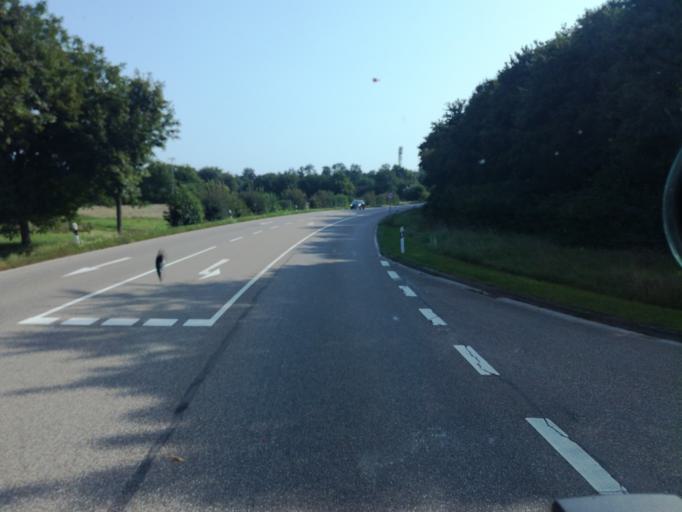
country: DE
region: Baden-Wuerttemberg
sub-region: Karlsruhe Region
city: Rheinau
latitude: 48.8756
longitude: 8.1874
